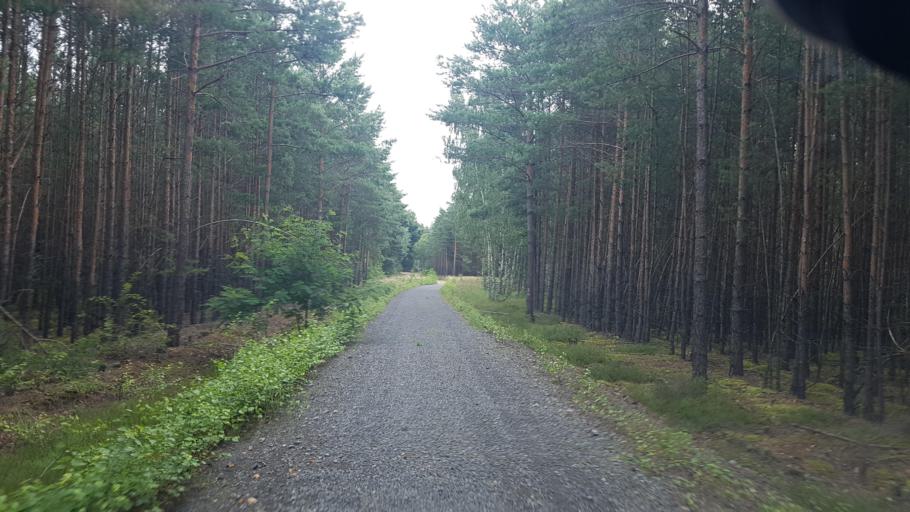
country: DE
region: Brandenburg
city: Altdobern
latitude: 51.6305
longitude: 13.9932
